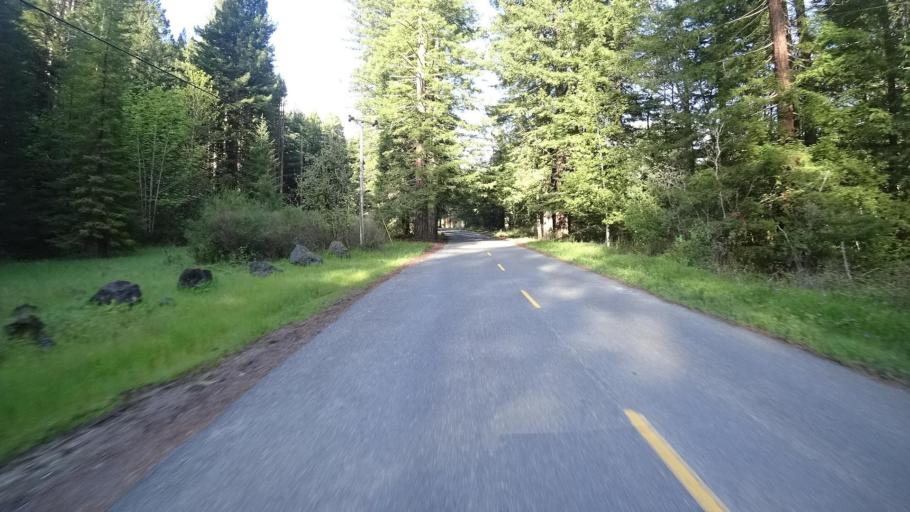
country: US
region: California
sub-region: Humboldt County
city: Rio Dell
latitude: 40.3506
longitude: -124.0085
